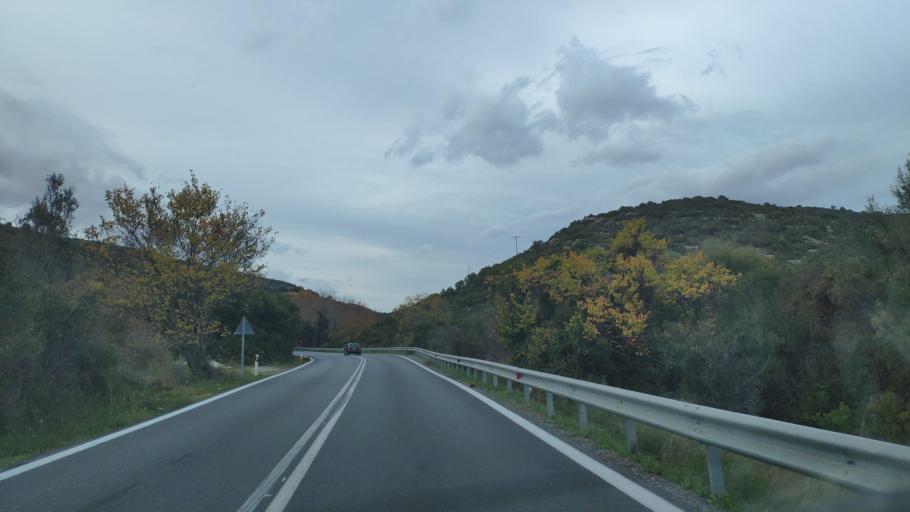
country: GR
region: Peloponnese
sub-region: Nomos Korinthias
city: Ayios Vasilios
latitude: 37.7642
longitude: 22.7301
